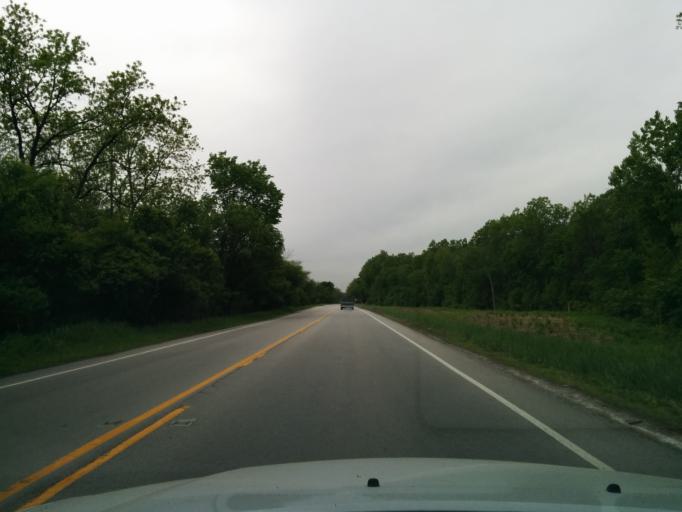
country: US
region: Illinois
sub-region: Cook County
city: Palos Park
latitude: 41.6831
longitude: -87.8415
